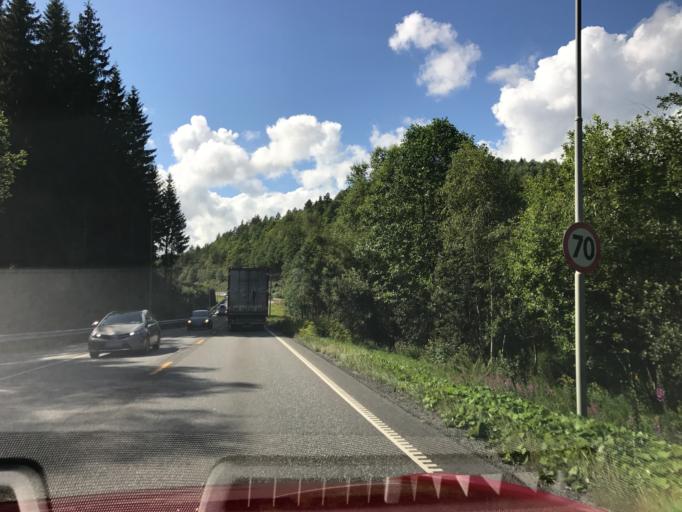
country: NO
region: Telemark
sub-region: Bamble
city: Herre
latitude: 58.9735
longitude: 9.5271
